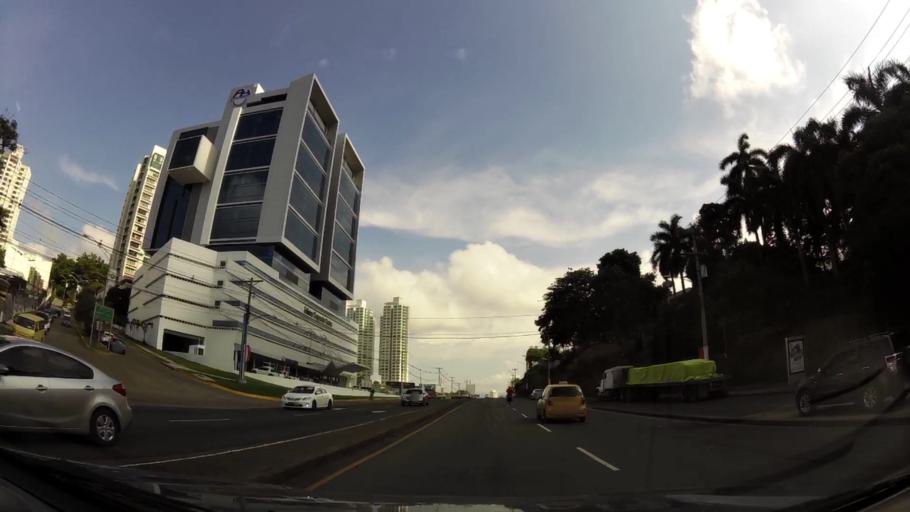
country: PA
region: Panama
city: Panama
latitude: 8.9909
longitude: -79.5313
